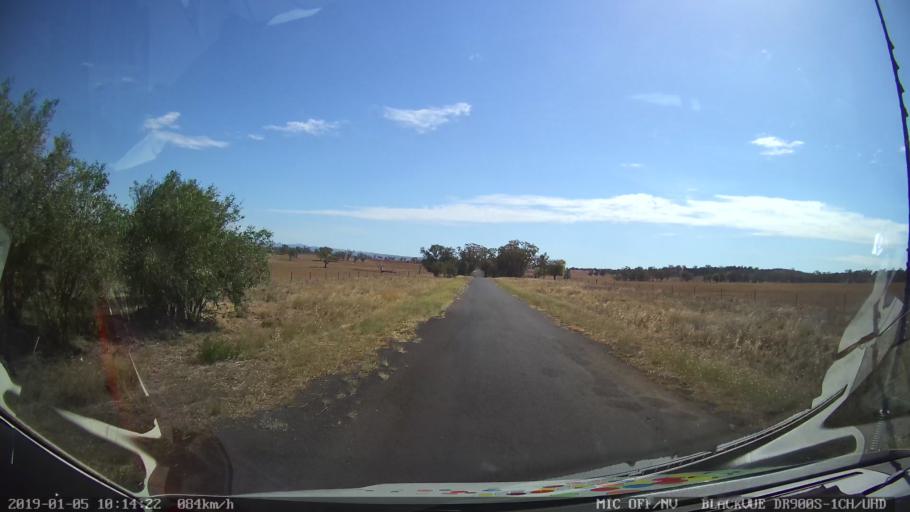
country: AU
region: New South Wales
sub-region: Gilgandra
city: Gilgandra
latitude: -31.5935
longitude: 148.9338
